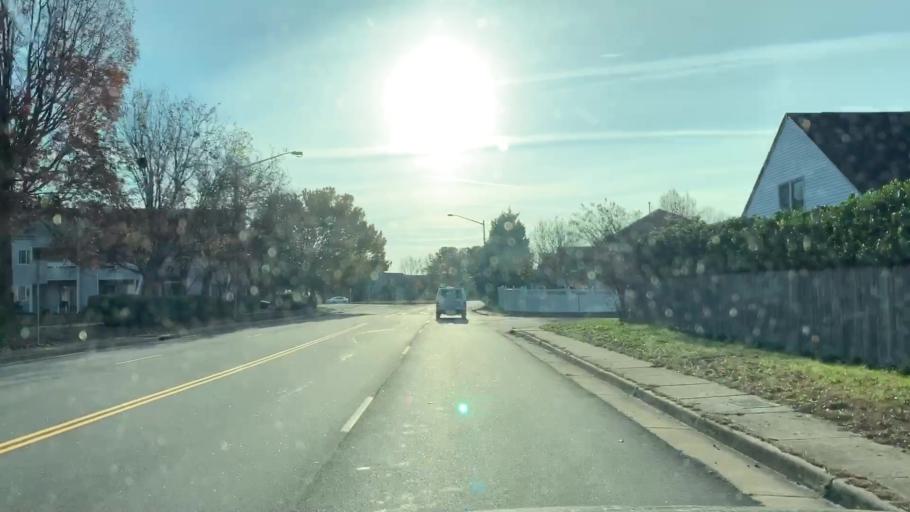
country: US
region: Virginia
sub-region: City of Chesapeake
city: Chesapeake
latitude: 36.7903
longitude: -76.1654
